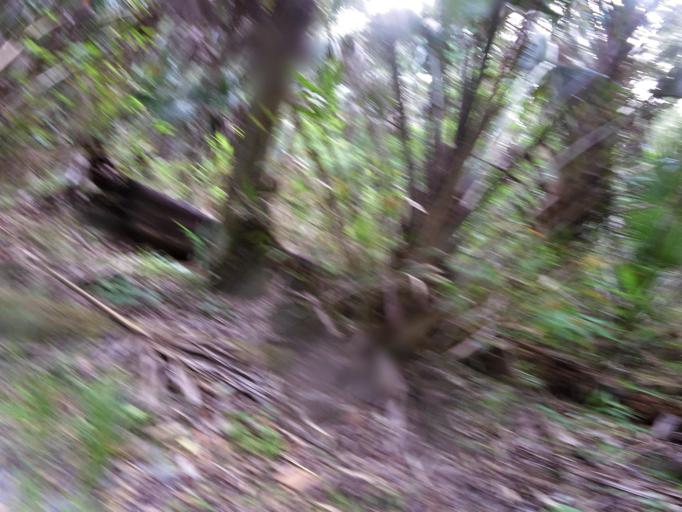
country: US
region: Florida
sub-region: Flagler County
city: Flagler Beach
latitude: 29.4213
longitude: -81.1402
